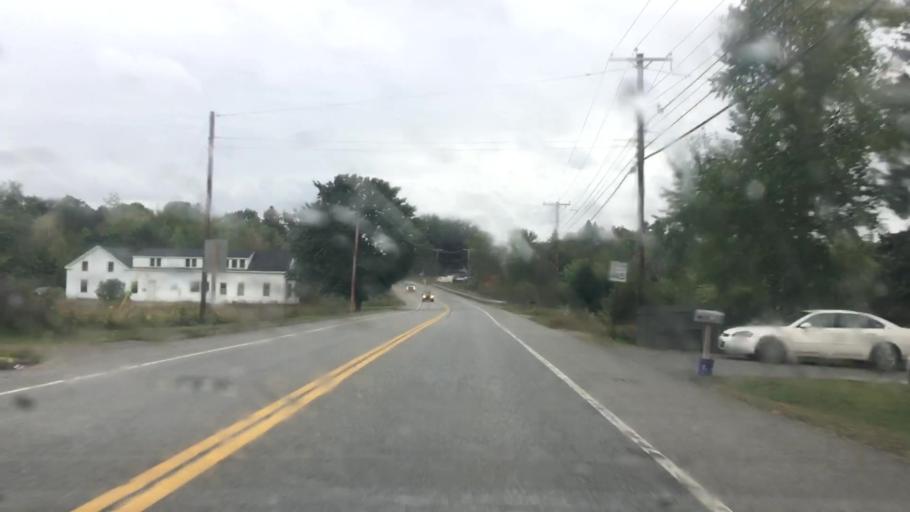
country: US
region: Maine
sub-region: Penobscot County
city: Orrington
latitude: 44.7261
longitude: -68.8271
